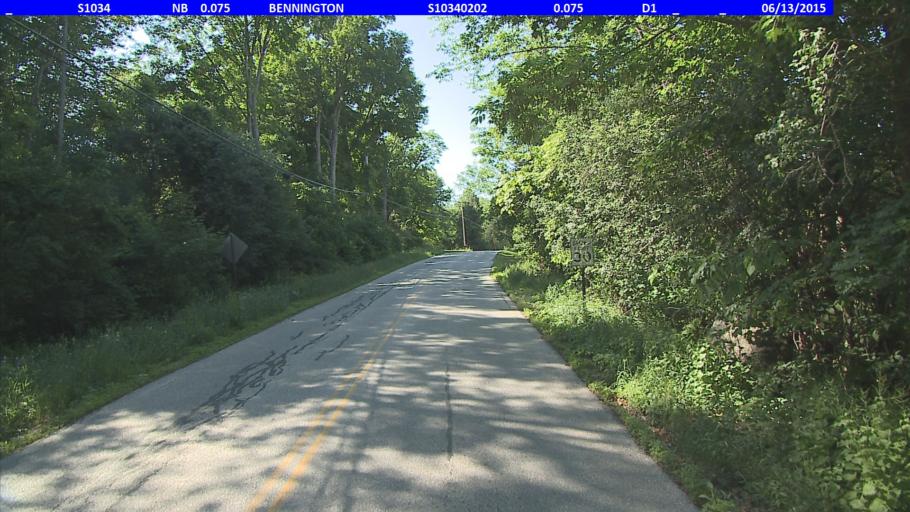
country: US
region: Vermont
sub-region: Bennington County
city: Bennington
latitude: 42.8535
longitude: -73.2052
